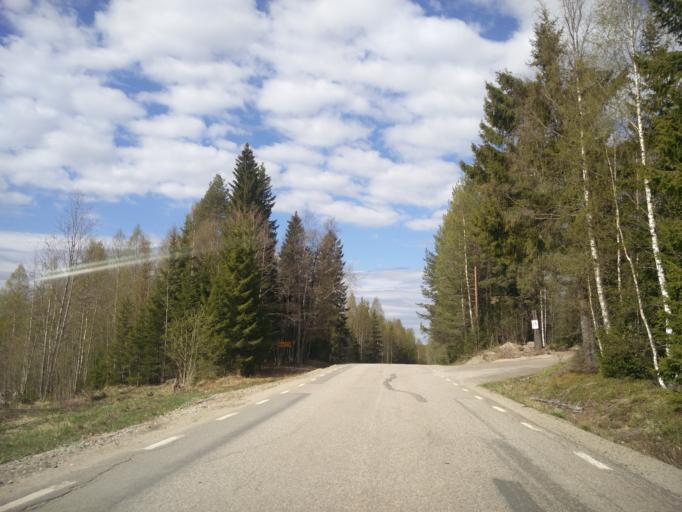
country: SE
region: Vaesternorrland
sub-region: Sundsvalls Kommun
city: Nolby
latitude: 62.2547
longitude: 17.2921
